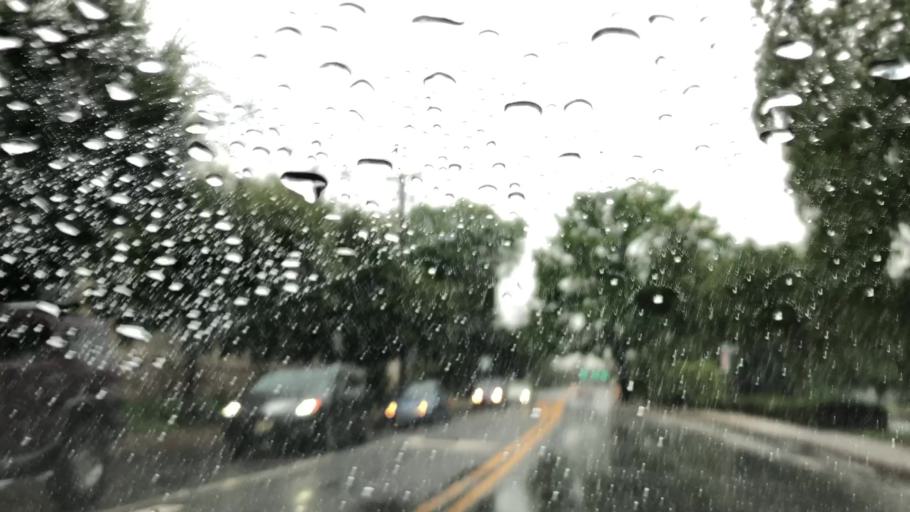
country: US
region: New Jersey
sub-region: Bergen County
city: Rochelle Park
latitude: 40.9122
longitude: -74.0777
